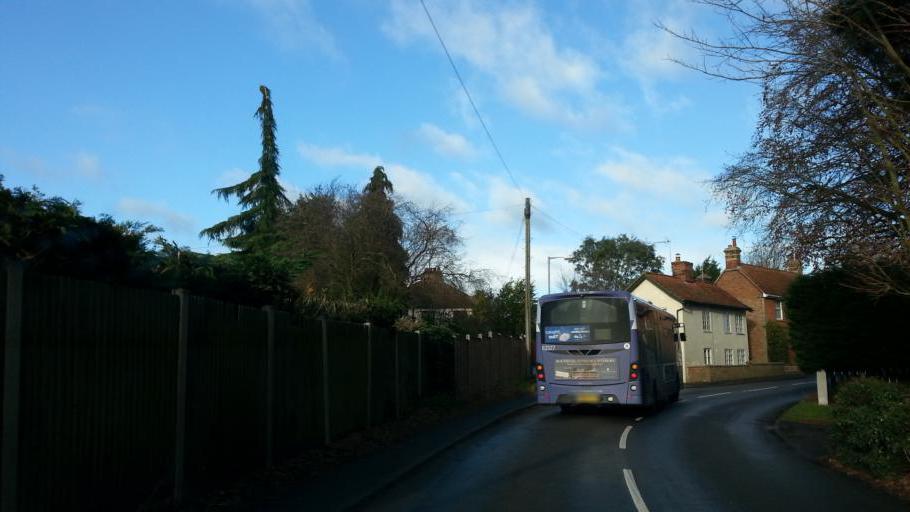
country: GB
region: England
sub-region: Norfolk
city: Ditchingham
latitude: 52.4657
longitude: 1.4416
